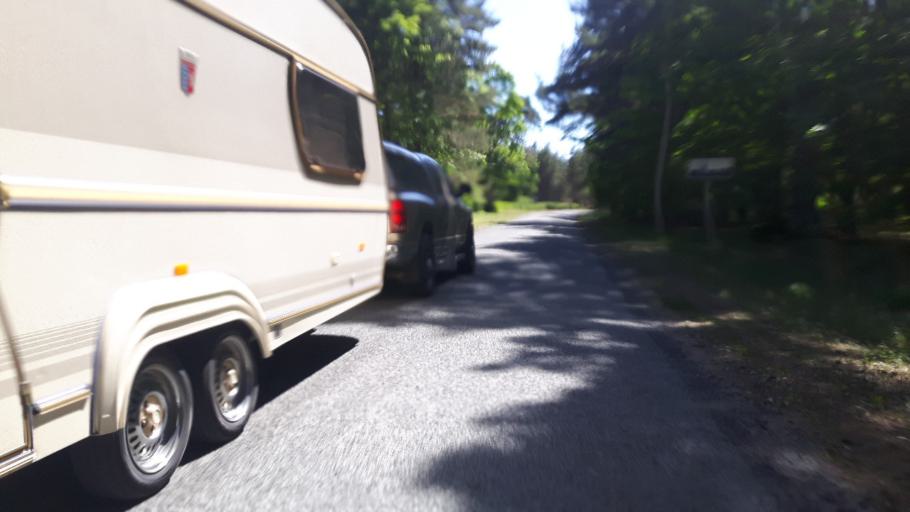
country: LV
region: Salacgrivas
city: Ainazi
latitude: 57.9249
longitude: 24.3905
